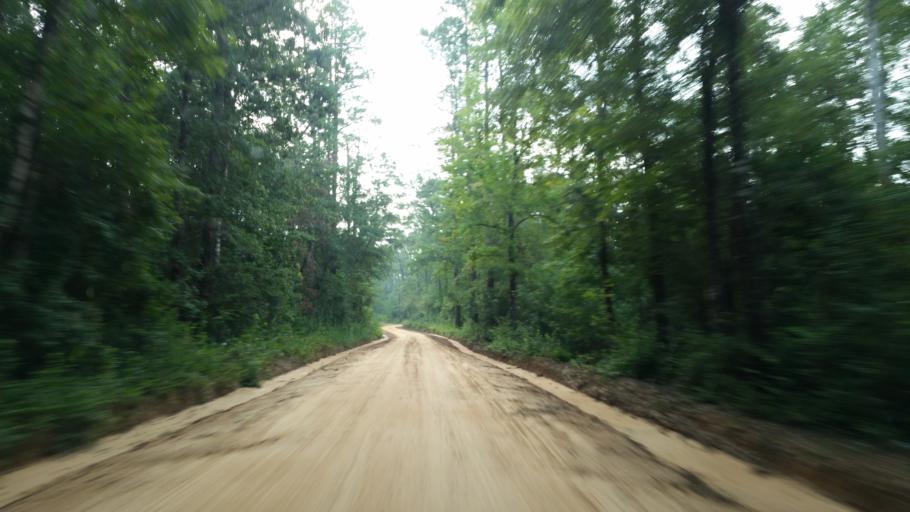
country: US
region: Alabama
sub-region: Baldwin County
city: Bay Minette
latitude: 30.7965
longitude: -87.5548
